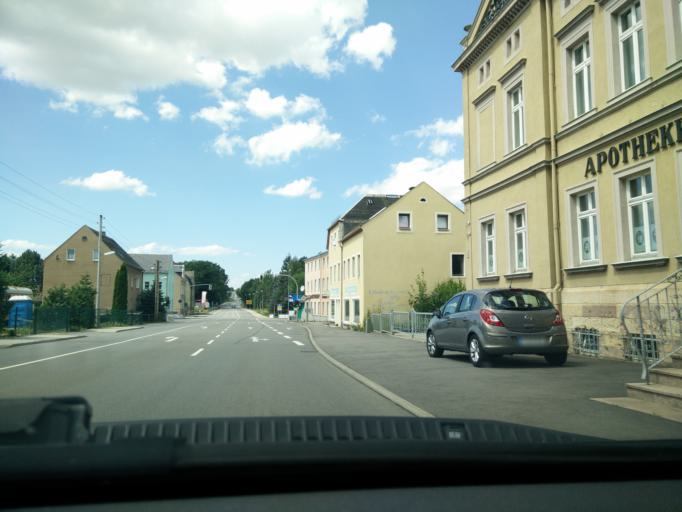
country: DE
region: Saxony
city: Hartmannsdorf
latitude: 50.8892
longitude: 12.7950
